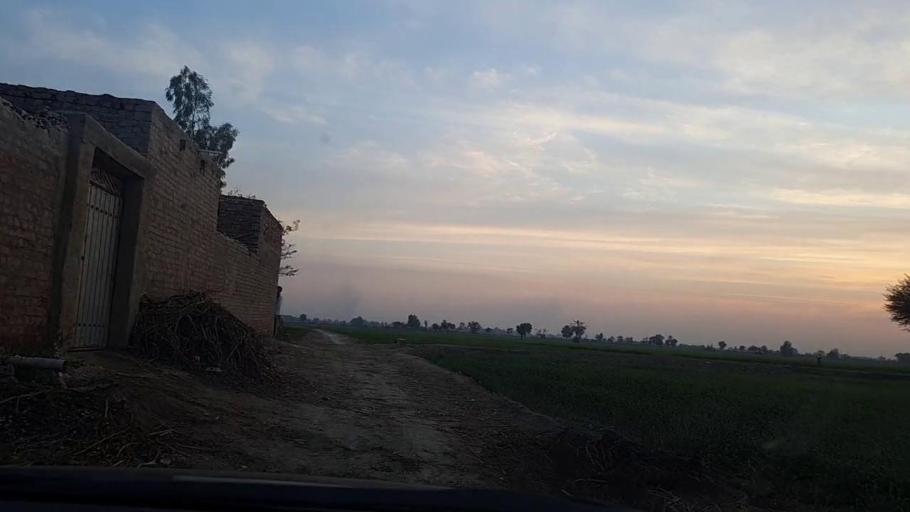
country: PK
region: Sindh
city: Sakrand
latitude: 26.2003
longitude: 68.3183
